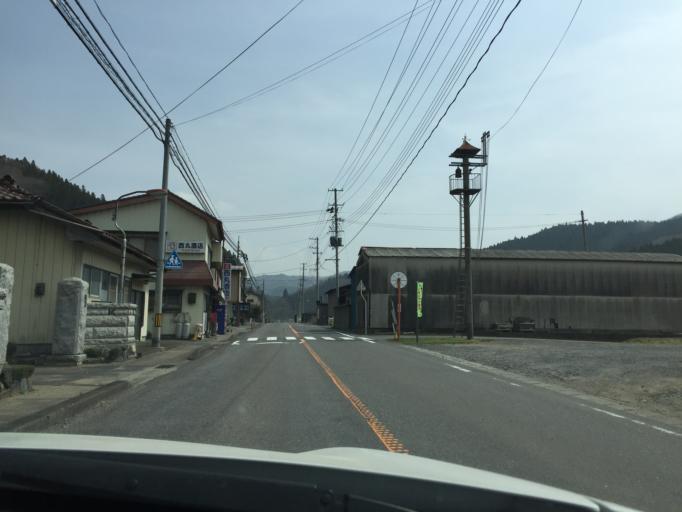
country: JP
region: Fukushima
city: Ishikawa
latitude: 37.0741
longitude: 140.5753
